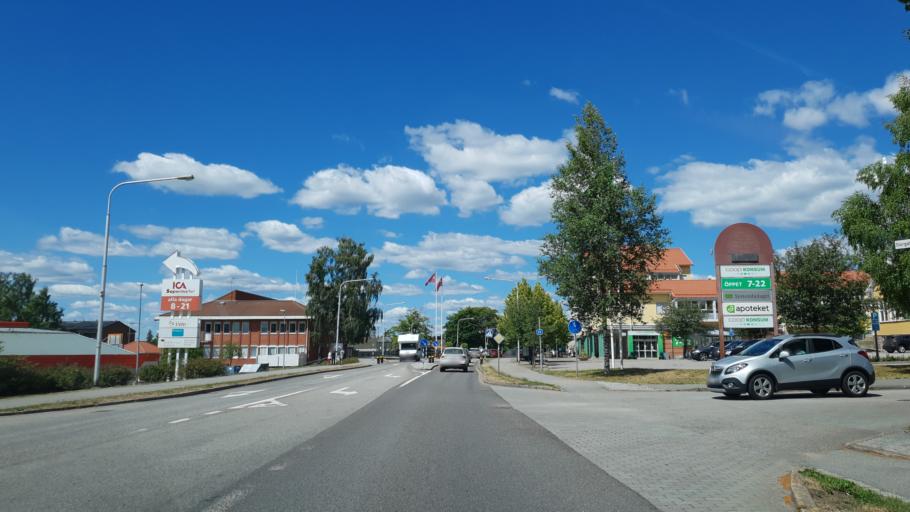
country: SE
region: Kronoberg
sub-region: Lessebo Kommun
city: Lessebo
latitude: 56.7504
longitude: 15.2707
